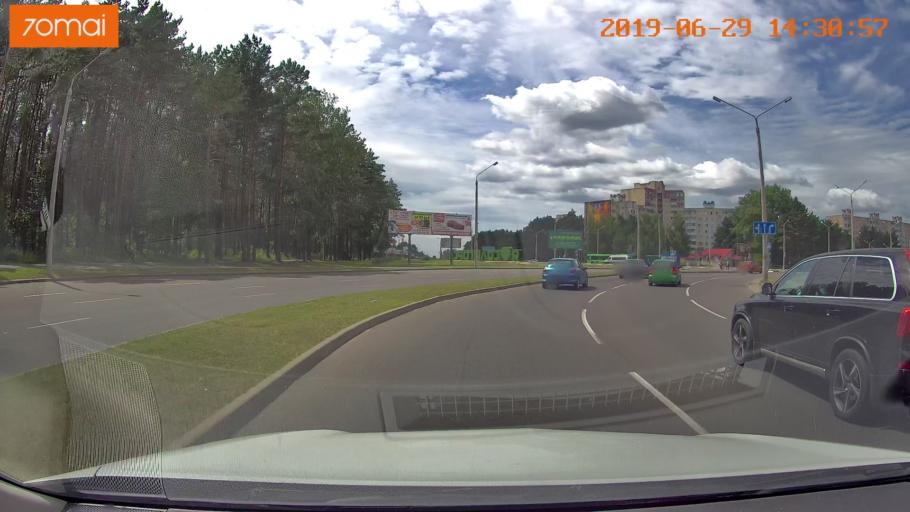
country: BY
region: Minsk
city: Salihorsk
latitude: 52.7815
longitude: 27.5119
